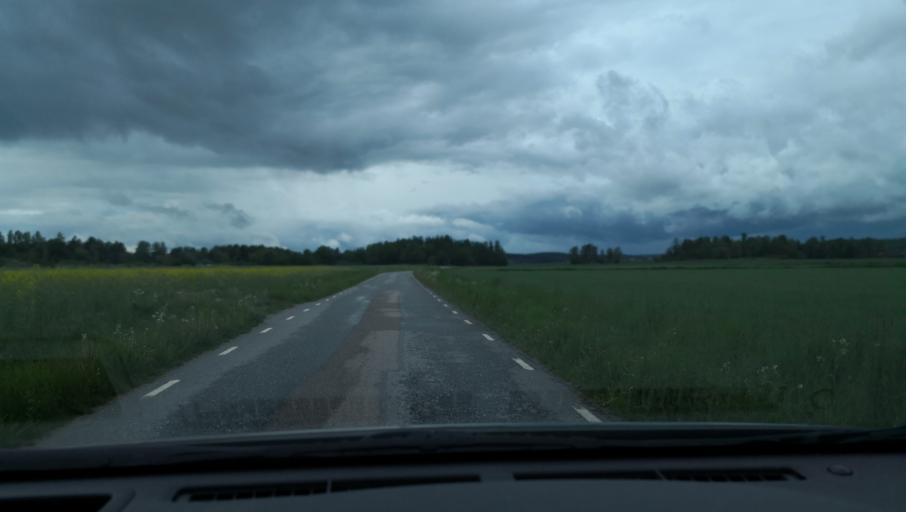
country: SE
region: Uppsala
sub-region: Enkopings Kommun
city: Orsundsbro
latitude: 59.7263
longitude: 17.3634
